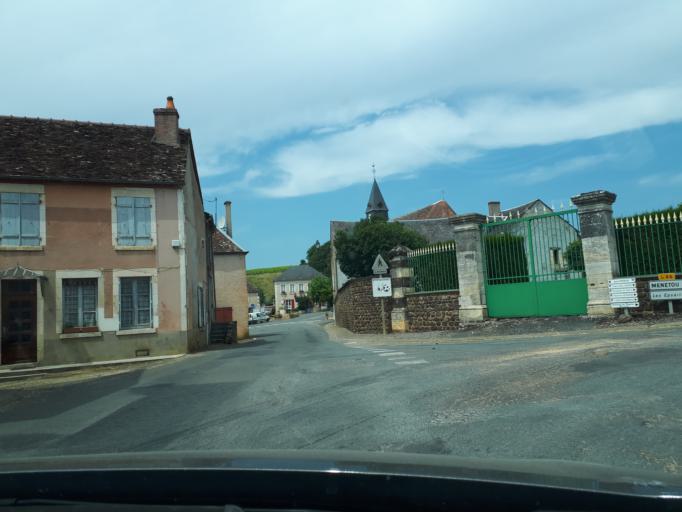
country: FR
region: Centre
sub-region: Departement du Cher
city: Sancerre
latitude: 47.3049
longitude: 2.7448
